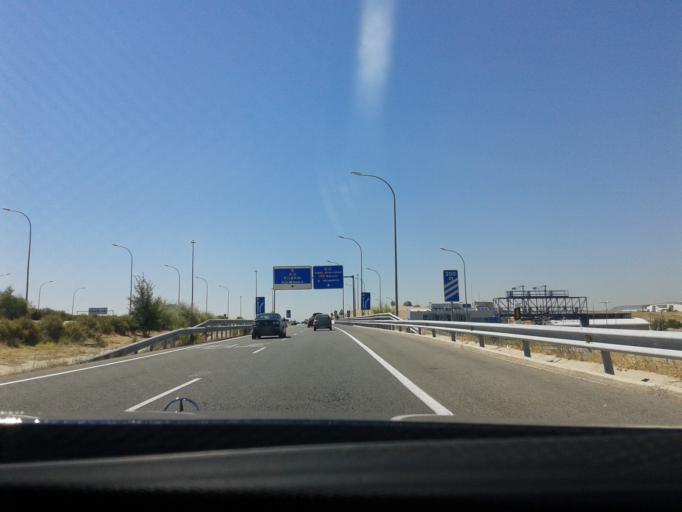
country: ES
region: Madrid
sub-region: Provincia de Madrid
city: Barajas de Madrid
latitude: 40.4816
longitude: -3.6025
